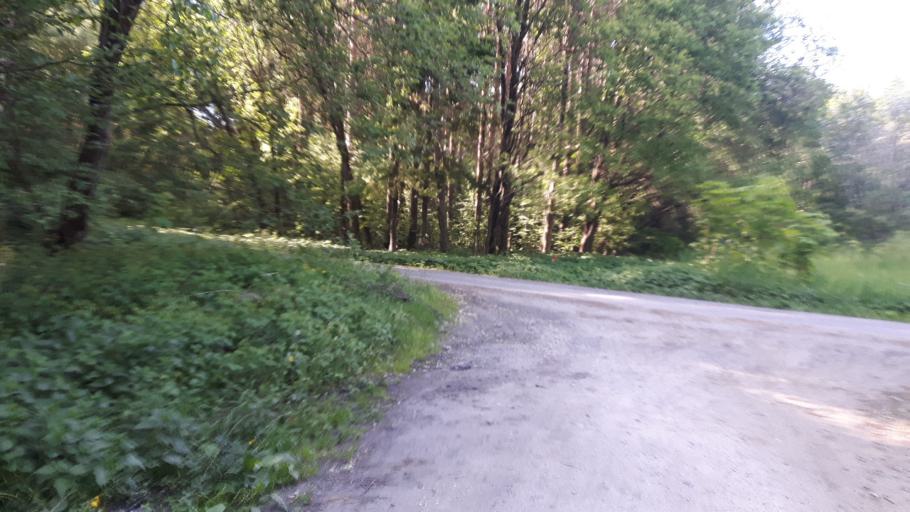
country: EE
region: Harju
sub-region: Tallinna linn
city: Kose
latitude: 59.4494
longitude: 24.9037
